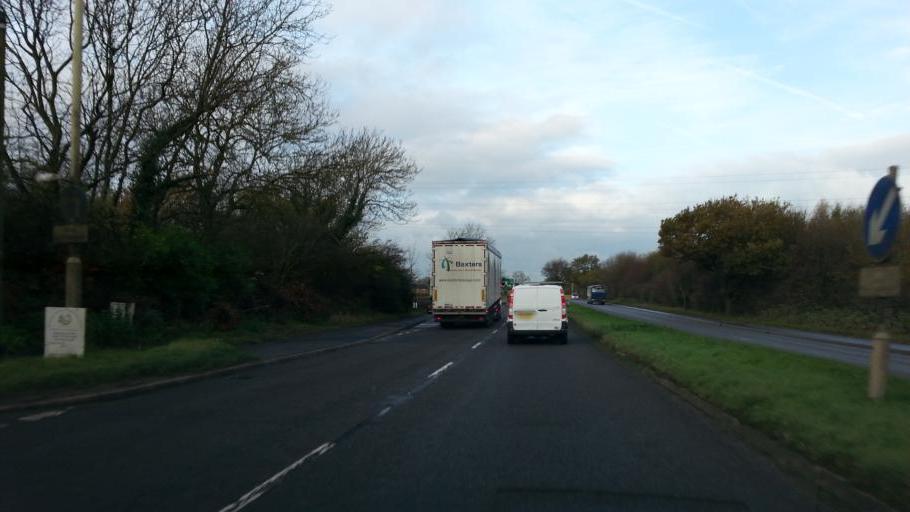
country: GB
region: England
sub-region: Leicestershire
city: Markfield
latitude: 52.7019
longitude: -1.3174
